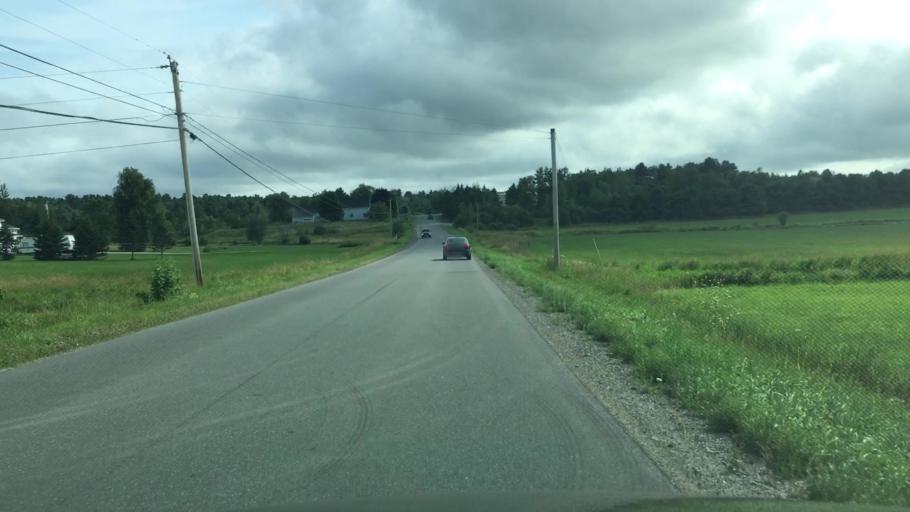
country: US
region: Maine
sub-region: Waldo County
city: Winterport
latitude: 44.6738
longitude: -68.8683
